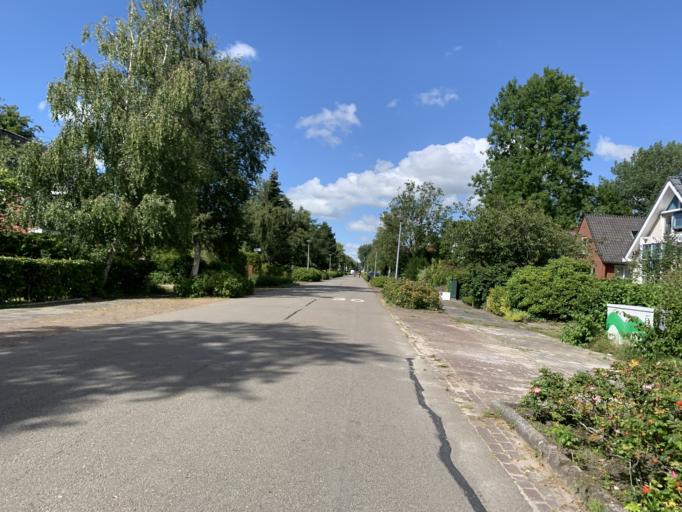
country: NL
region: Groningen
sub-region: Gemeente Groningen
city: Groningen
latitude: 53.1858
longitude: 6.5510
